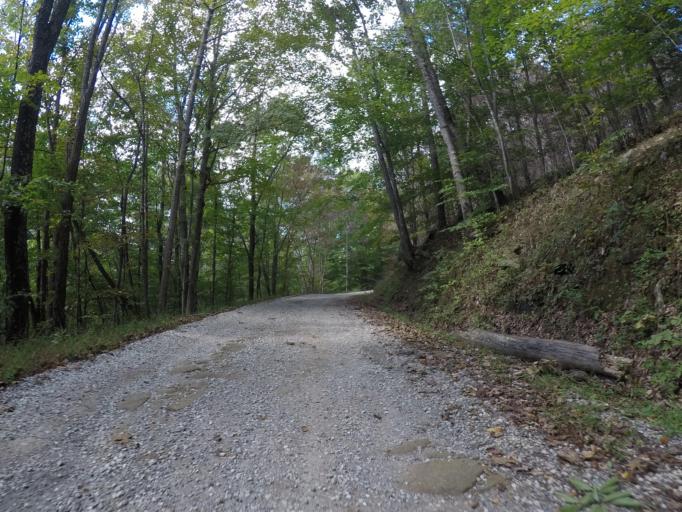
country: US
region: West Virginia
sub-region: Wayne County
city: Lavalette
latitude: 38.3536
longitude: -82.4571
